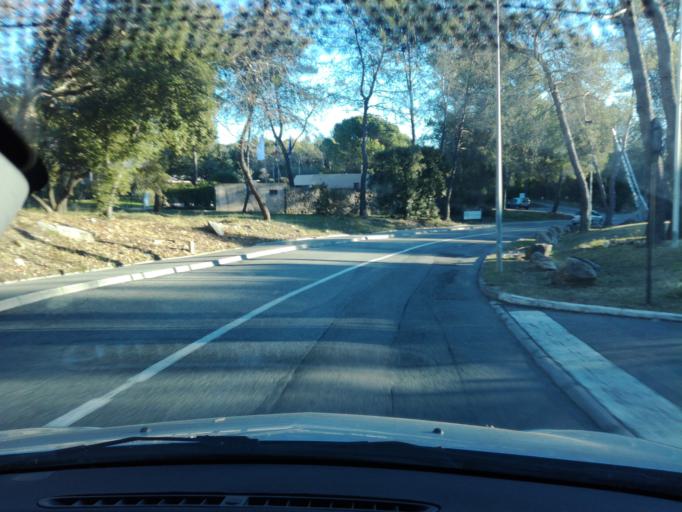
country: FR
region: Provence-Alpes-Cote d'Azur
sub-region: Departement des Alpes-Maritimes
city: Vallauris
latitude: 43.6142
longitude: 7.0588
